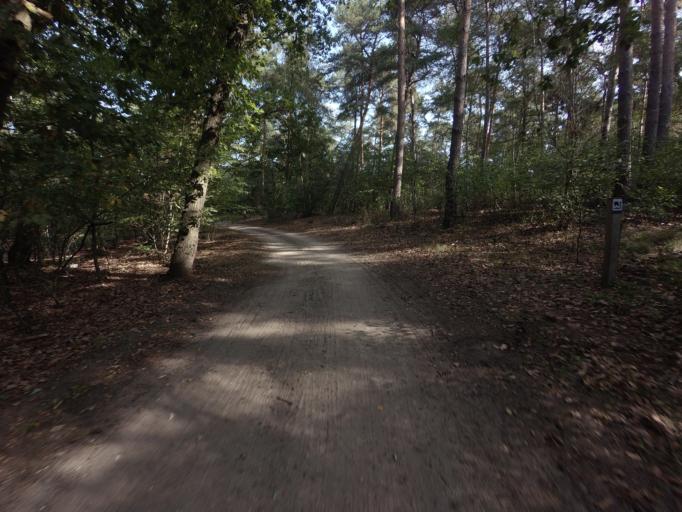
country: NL
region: Limburg
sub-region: Gemeente Roerdalen
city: Herkenbosch
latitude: 51.1730
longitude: 6.0817
